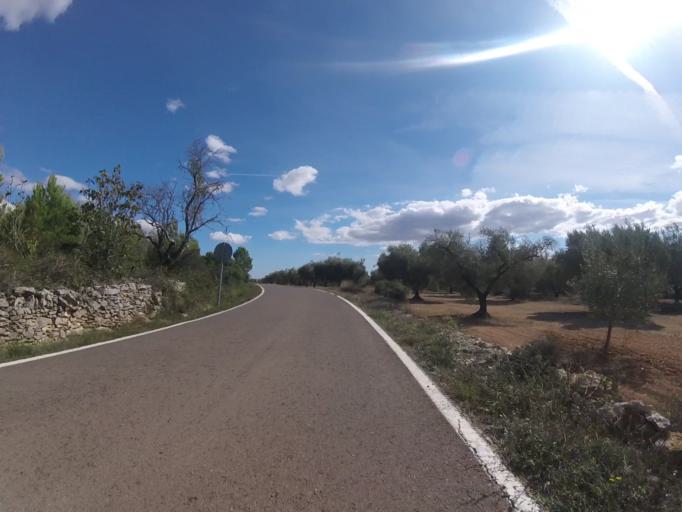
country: ES
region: Valencia
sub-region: Provincia de Castello
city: Albocasser
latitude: 40.4028
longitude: 0.0820
